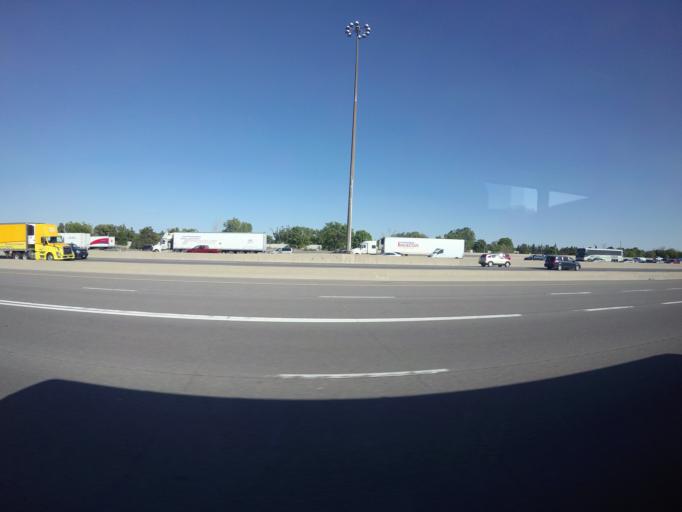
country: CA
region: Ontario
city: Pickering
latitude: 43.8202
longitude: -79.1105
